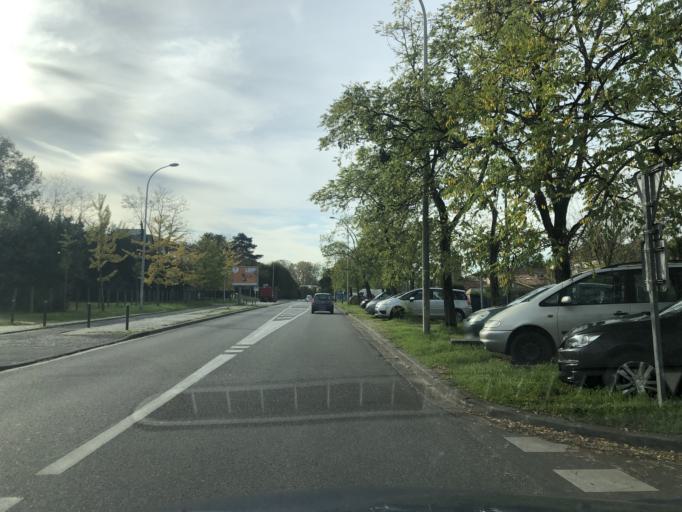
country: FR
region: Aquitaine
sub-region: Departement de la Gironde
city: Merignac
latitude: 44.8417
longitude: -0.6395
